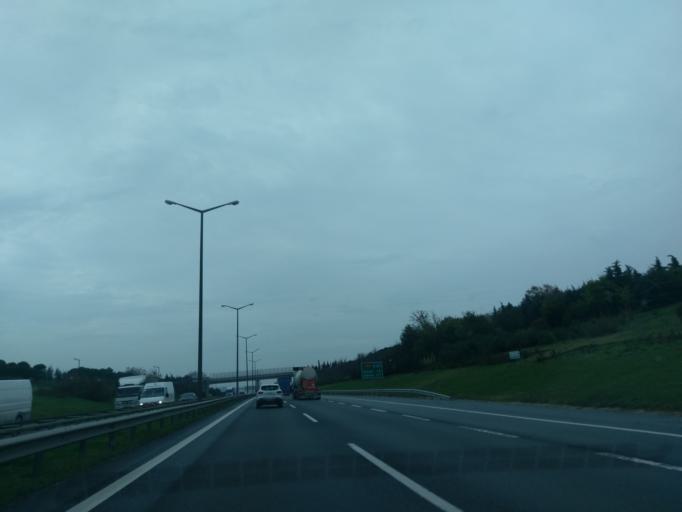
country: TR
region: Istanbul
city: Silivri
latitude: 41.1118
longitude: 28.2641
